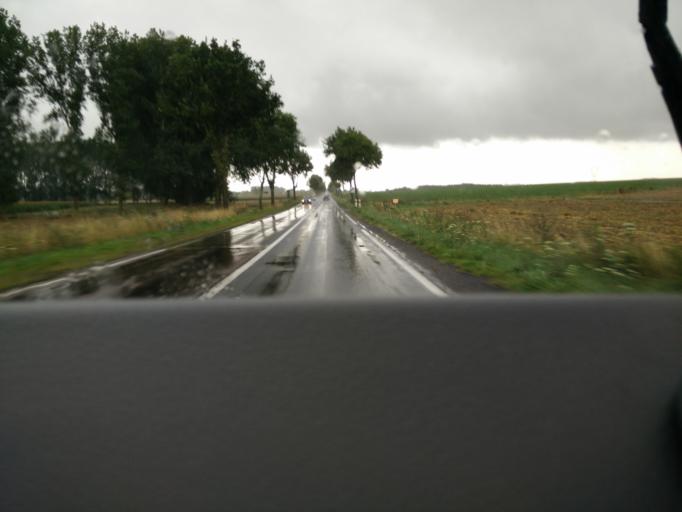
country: FR
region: Nord-Pas-de-Calais
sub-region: Departement du Pas-de-Calais
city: Savy-Berlette
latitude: 50.3532
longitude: 2.4955
